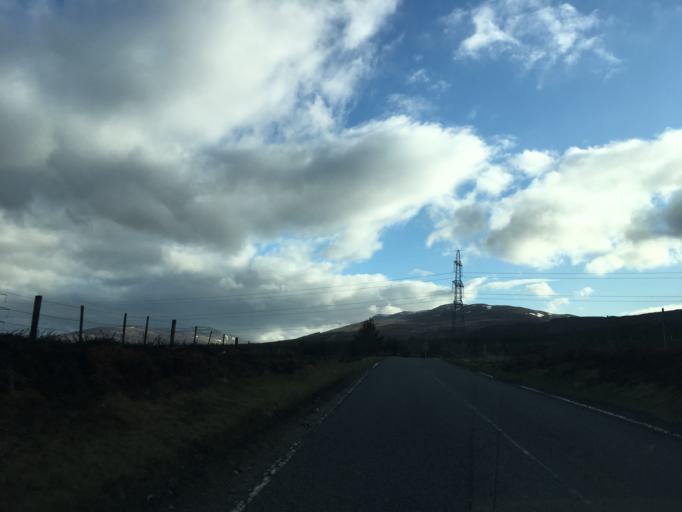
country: GB
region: Scotland
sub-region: Highland
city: Kingussie
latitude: 56.9644
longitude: -4.2405
